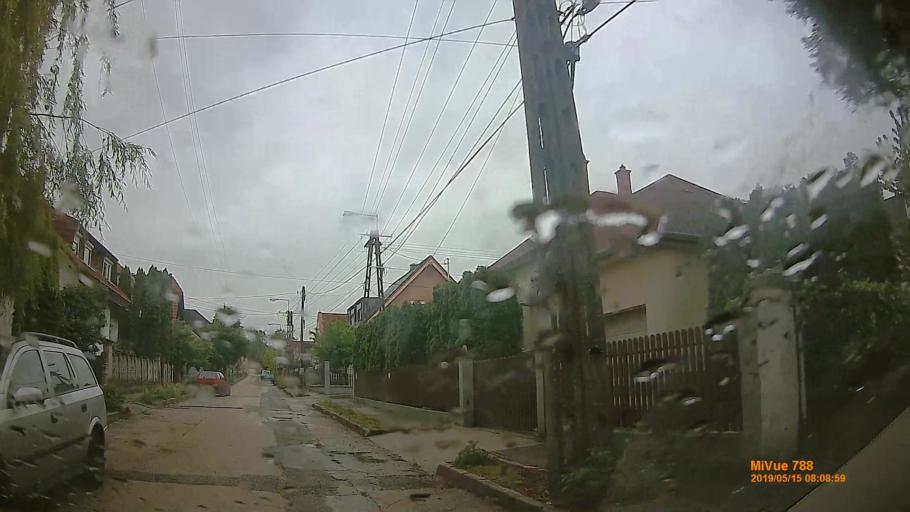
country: HU
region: Veszprem
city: Veszprem
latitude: 47.0995
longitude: 17.9206
